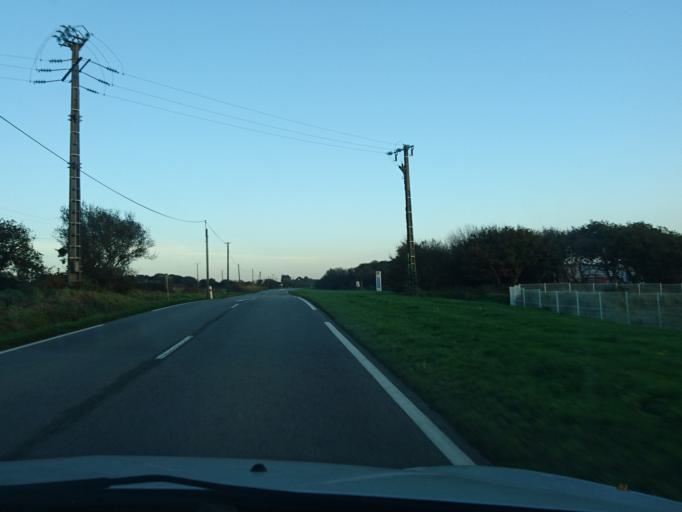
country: FR
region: Brittany
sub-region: Departement du Finistere
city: Lanrivoare
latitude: 48.4730
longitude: -4.6489
